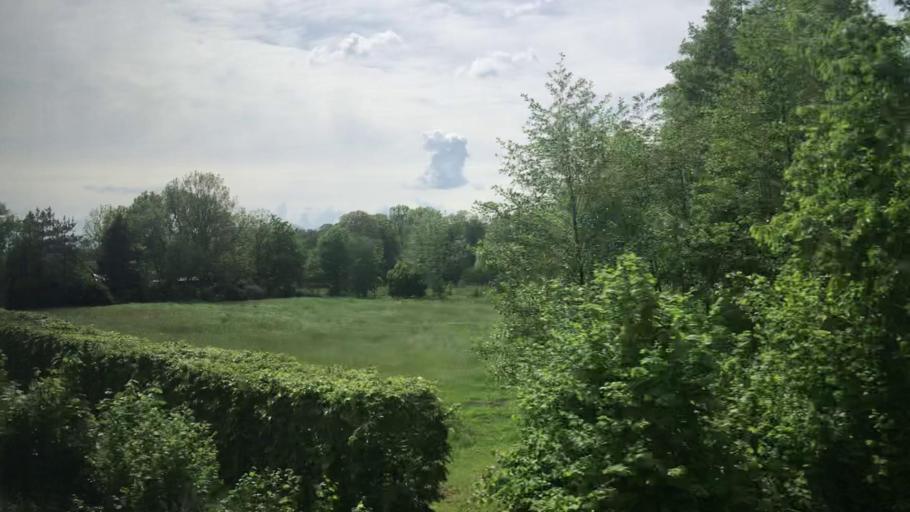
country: PL
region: Lower Silesian Voivodeship
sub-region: Powiat wroclawski
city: Katy Wroclawskie
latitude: 51.0082
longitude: 16.6962
